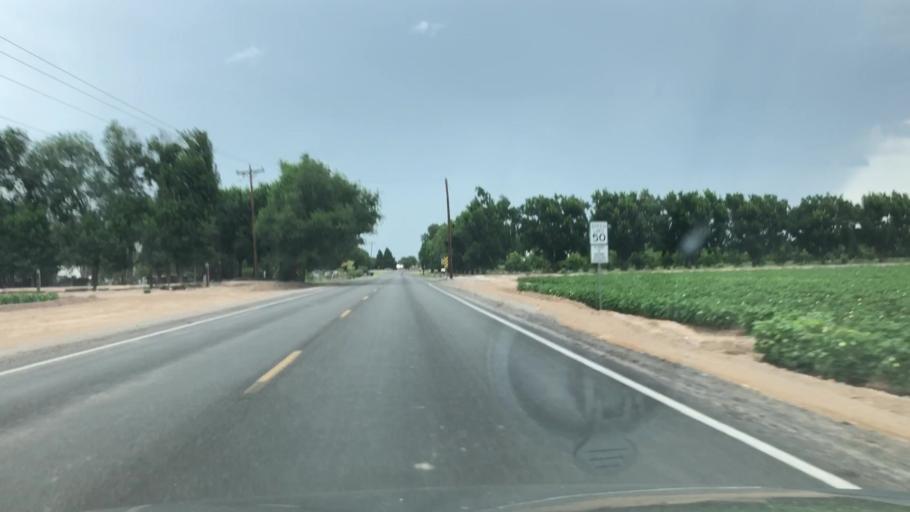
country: US
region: New Mexico
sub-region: Dona Ana County
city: La Union
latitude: 31.9794
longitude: -106.6514
